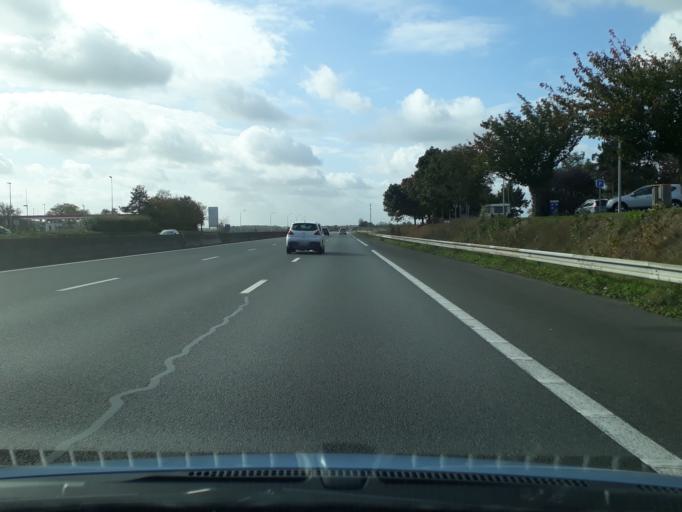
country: FR
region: Centre
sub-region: Departement du Loir-et-Cher
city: La Chaussee-Saint-Victor
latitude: 47.6648
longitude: 1.3876
